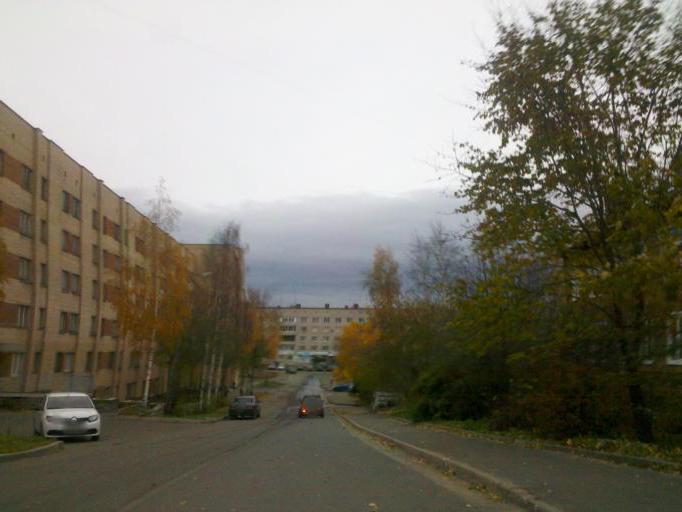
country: RU
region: Republic of Karelia
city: Petrozavodsk
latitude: 61.7763
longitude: 34.3804
